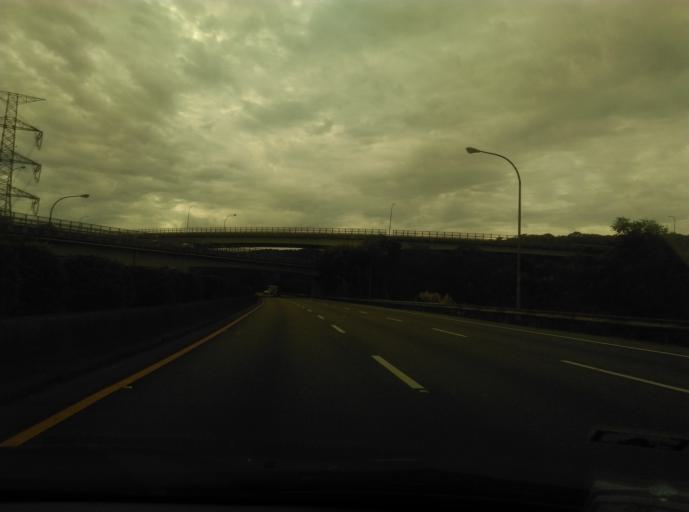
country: TW
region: Taiwan
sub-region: Taoyuan
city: Taoyuan
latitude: 24.9396
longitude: 121.3267
